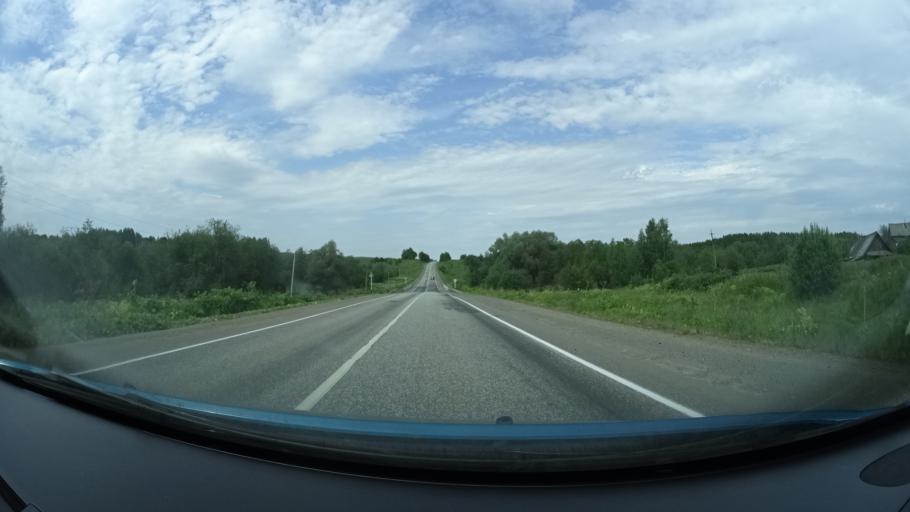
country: RU
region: Perm
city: Osa
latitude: 57.1464
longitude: 55.5291
